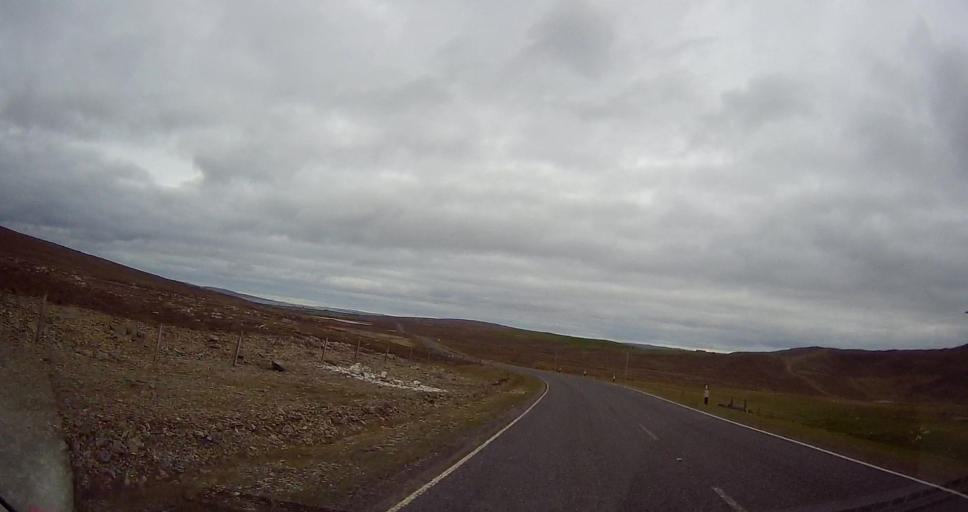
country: GB
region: Scotland
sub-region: Shetland Islands
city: Shetland
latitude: 60.7239
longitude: -0.9071
